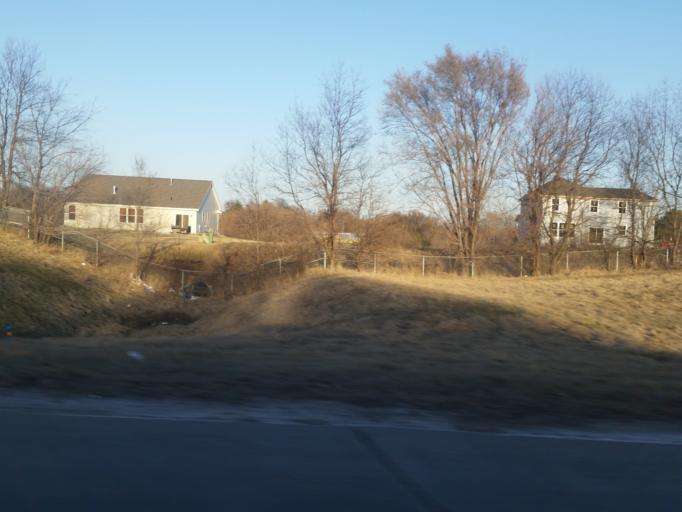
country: US
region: Nebraska
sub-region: Sarpy County
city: Offutt Air Force Base
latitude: 41.1740
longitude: -95.9397
